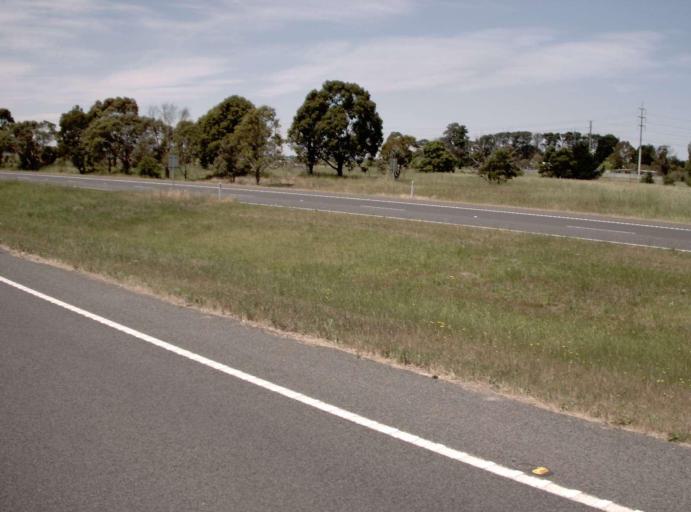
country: AU
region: Victoria
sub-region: Latrobe
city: Morwell
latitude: -38.2410
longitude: 146.4464
